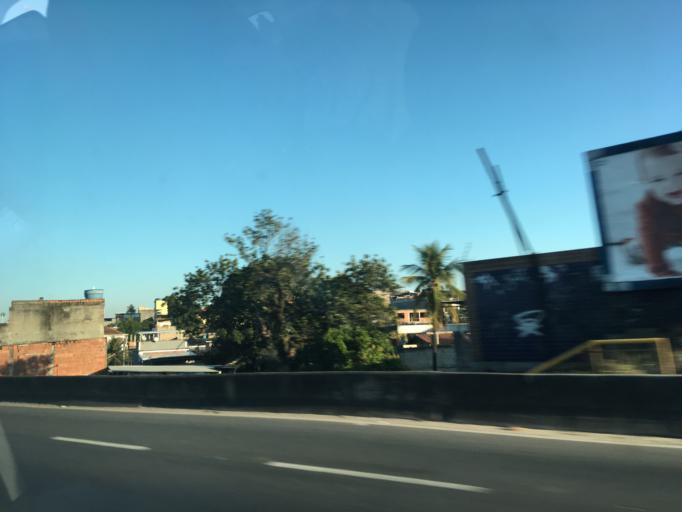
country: BR
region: Rio de Janeiro
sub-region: Sao Joao De Meriti
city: Sao Joao de Meriti
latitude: -22.7854
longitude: -43.3798
